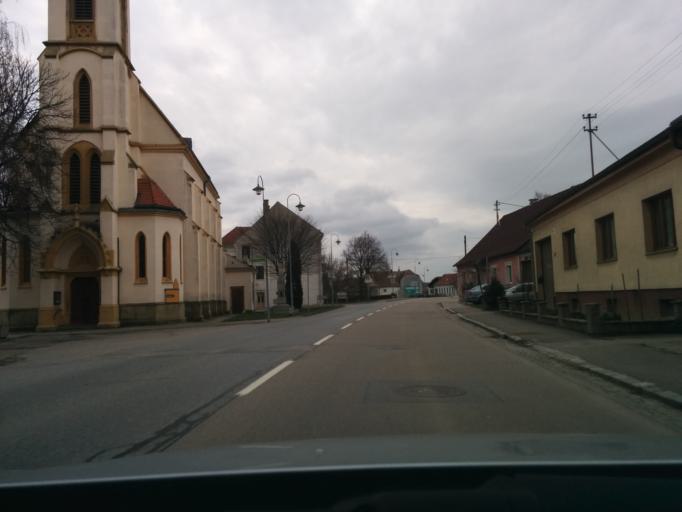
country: AT
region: Lower Austria
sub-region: Politischer Bezirk Mistelbach
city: Asparn an der Zaya
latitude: 48.6072
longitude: 16.5404
